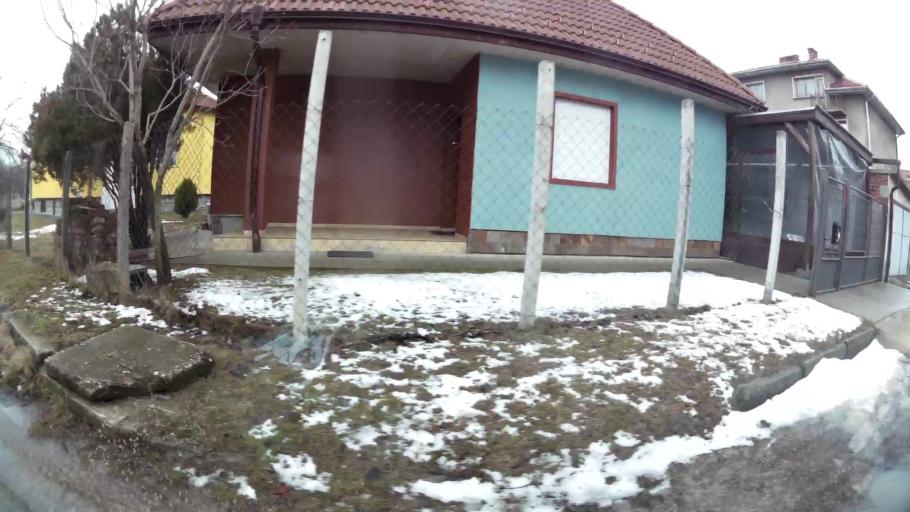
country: BG
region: Sofiya
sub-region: Obshtina Bozhurishte
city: Bozhurishte
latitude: 42.7420
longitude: 23.2690
